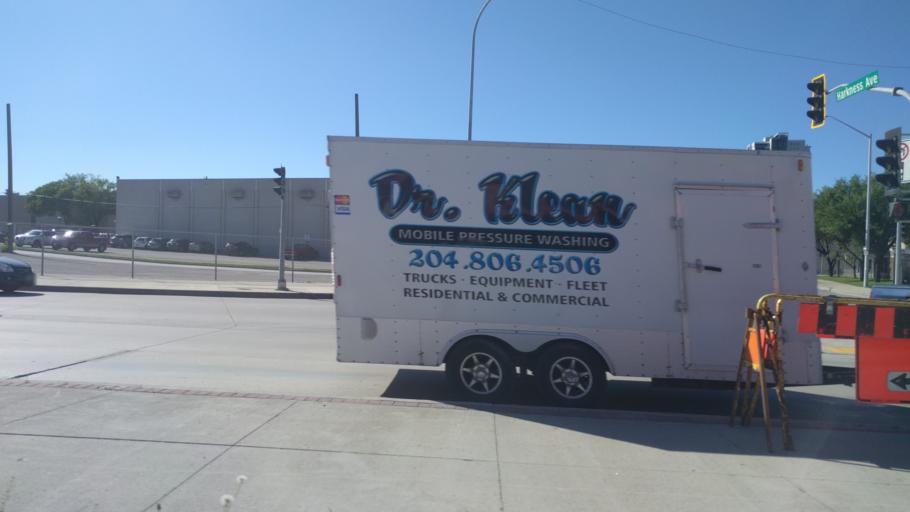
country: CA
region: Manitoba
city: Winnipeg
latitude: 49.8813
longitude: -97.1344
